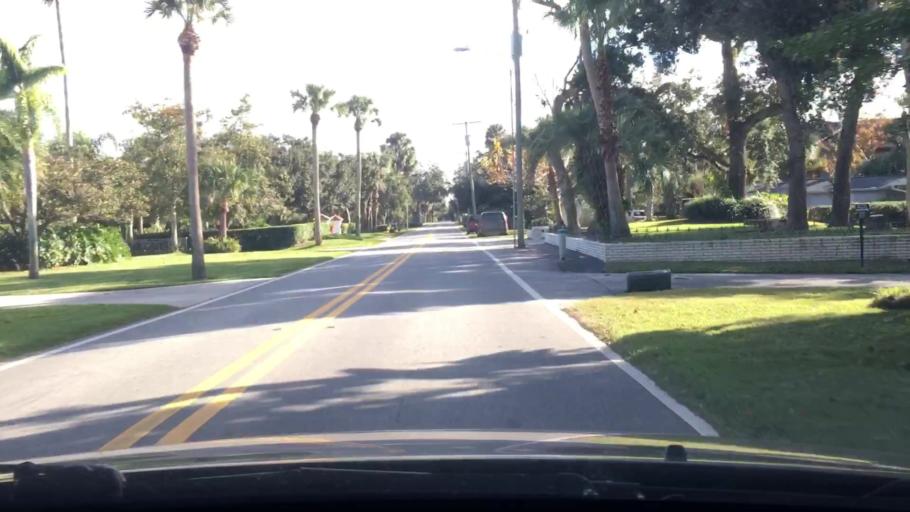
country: US
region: Florida
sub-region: Volusia County
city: Ormond Beach
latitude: 29.3128
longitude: -81.0585
